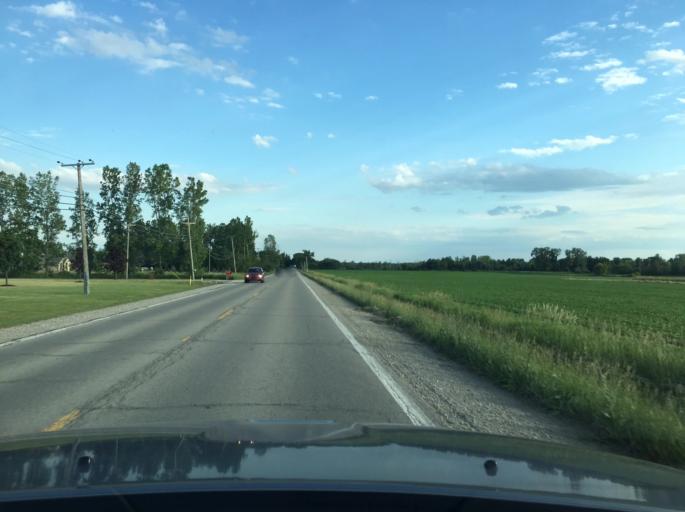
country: US
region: Michigan
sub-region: Macomb County
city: Romeo
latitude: 42.7860
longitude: -82.9619
